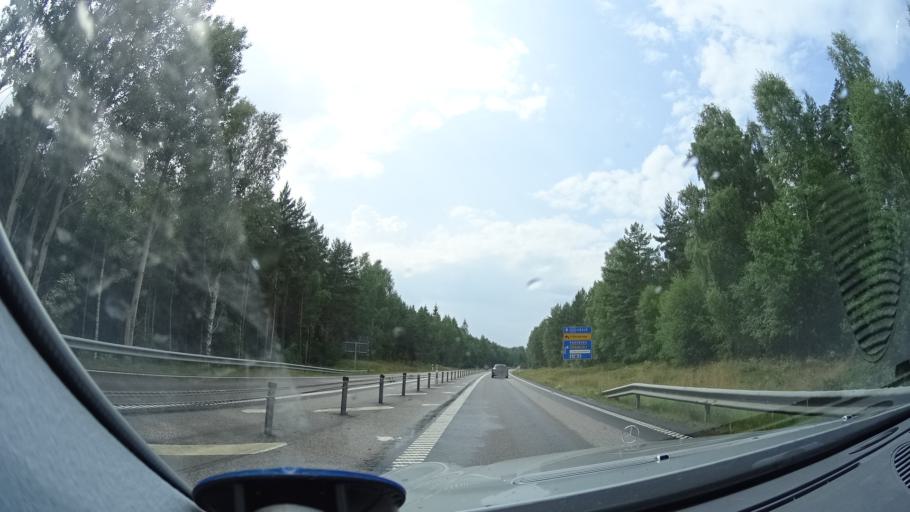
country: SE
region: Kalmar
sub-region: Nybro Kommun
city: Nybro
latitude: 56.7282
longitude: 15.9241
